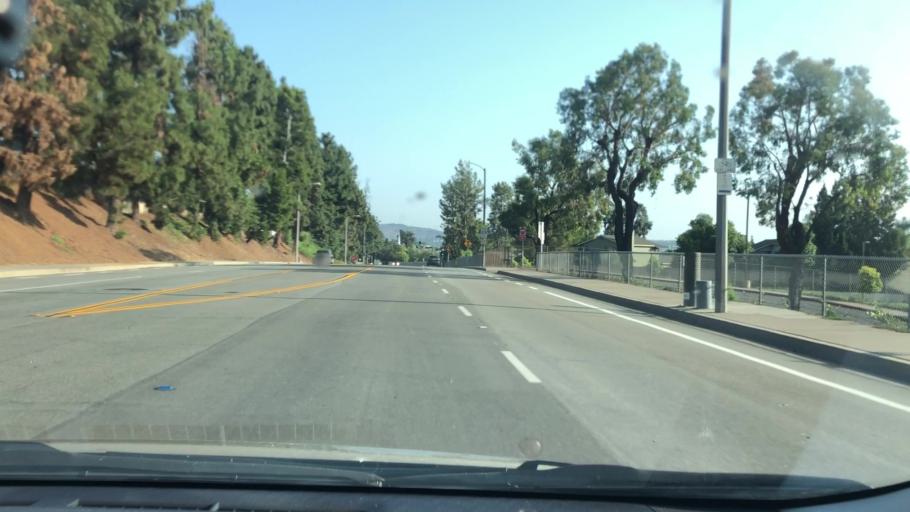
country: US
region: California
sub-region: Orange County
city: Yorba Linda
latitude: 33.8865
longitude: -117.7902
